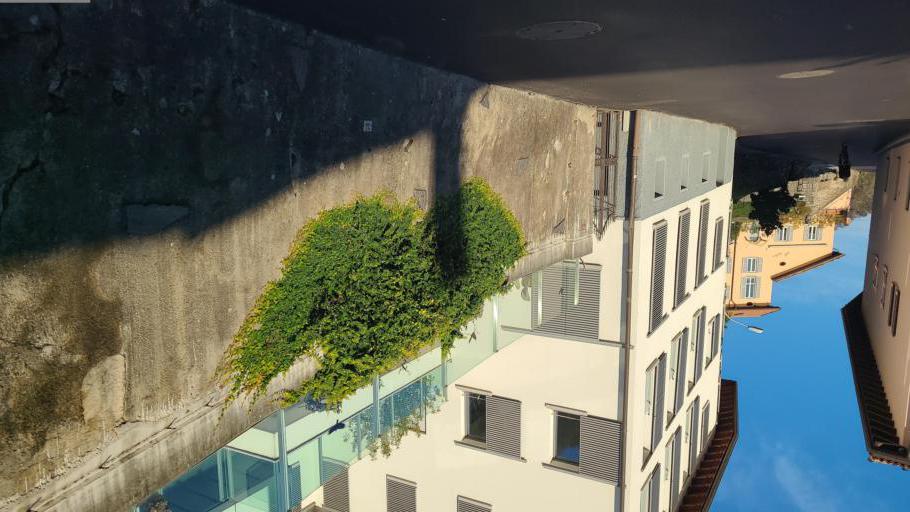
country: IT
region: Lombardy
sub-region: Provincia di Varese
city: Brusimpiano
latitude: 45.9496
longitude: 8.9058
